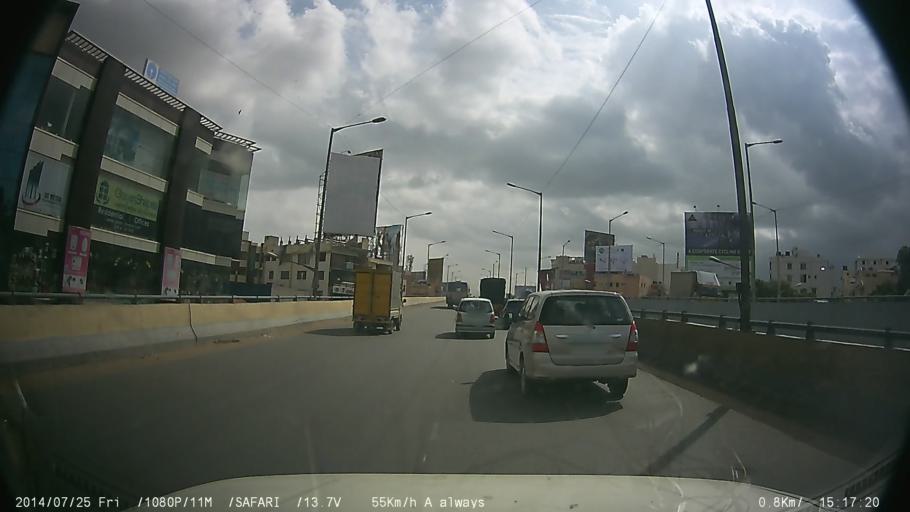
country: IN
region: Karnataka
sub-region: Bangalore Urban
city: Bangalore
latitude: 12.9267
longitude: 77.6783
